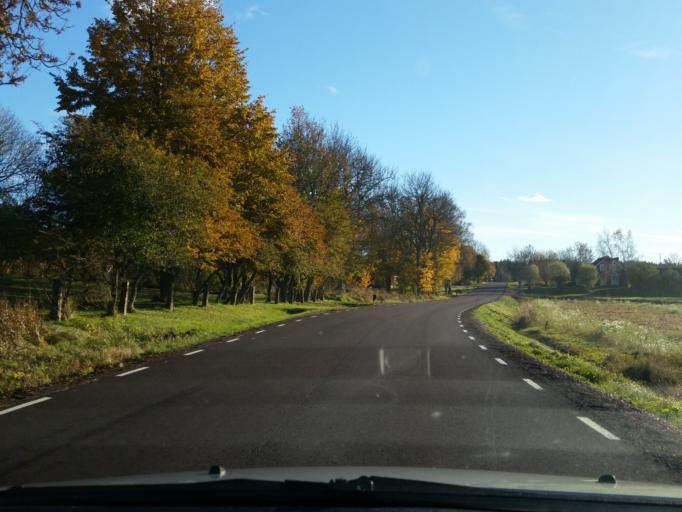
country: AX
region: Alands landsbygd
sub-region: Jomala
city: Jomala
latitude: 60.1876
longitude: 19.9612
